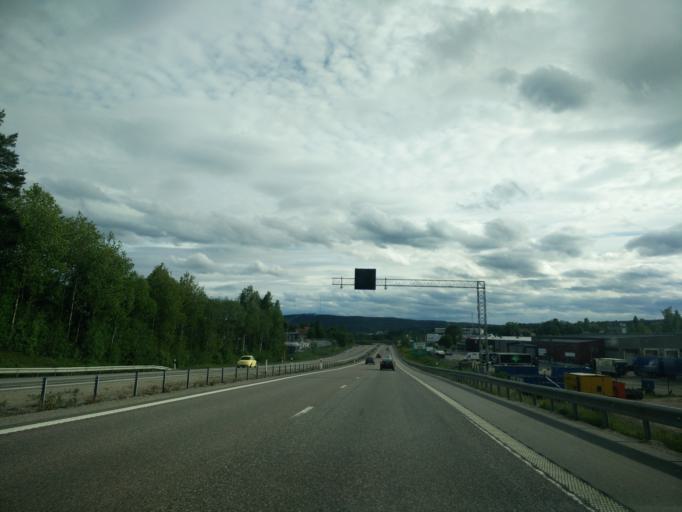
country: SE
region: Vaesternorrland
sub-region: Sundsvalls Kommun
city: Johannedal
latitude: 62.4196
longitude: 17.3465
